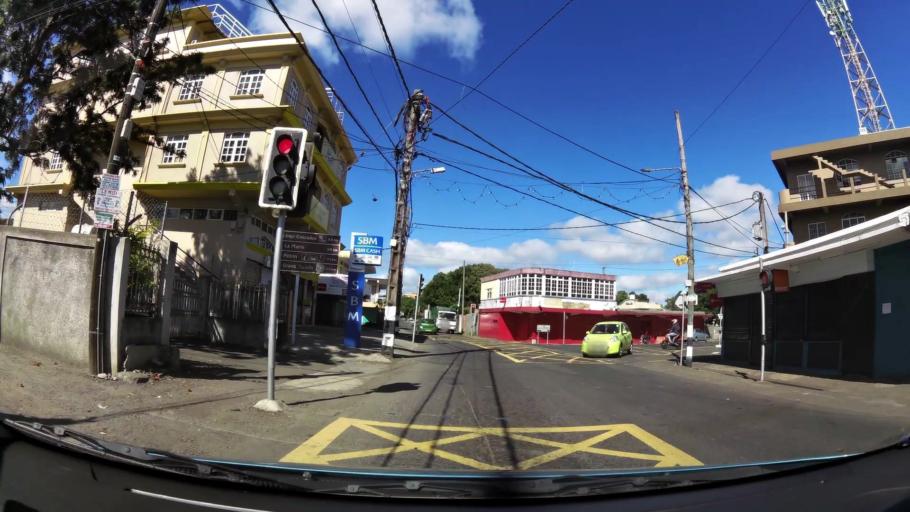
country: MU
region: Plaines Wilhems
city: Vacoas
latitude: -20.3227
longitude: 57.4848
